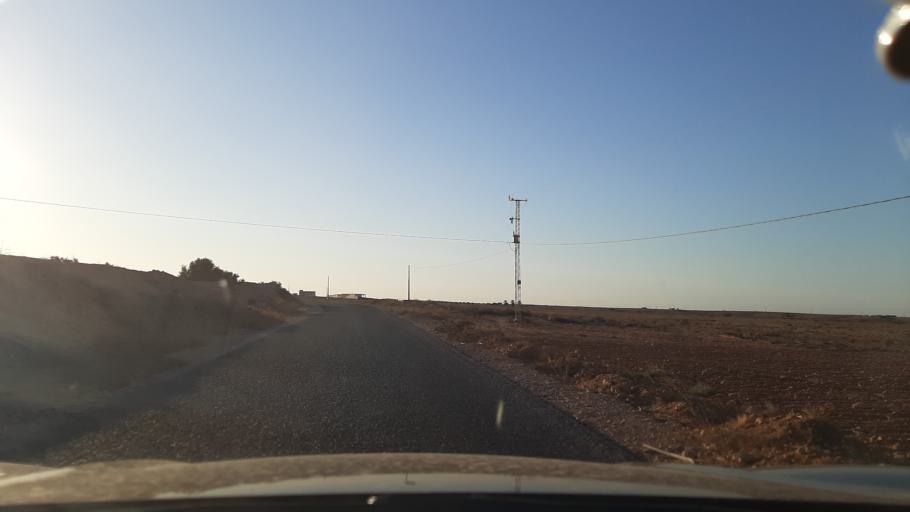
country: TN
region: Qabis
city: Matmata
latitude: 33.6205
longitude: 10.1435
